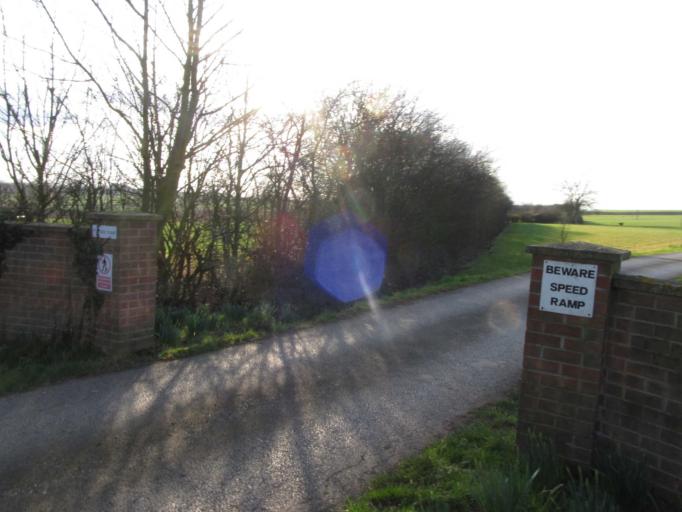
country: GB
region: England
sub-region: Nottinghamshire
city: Misterton
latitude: 53.3781
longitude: -0.8627
